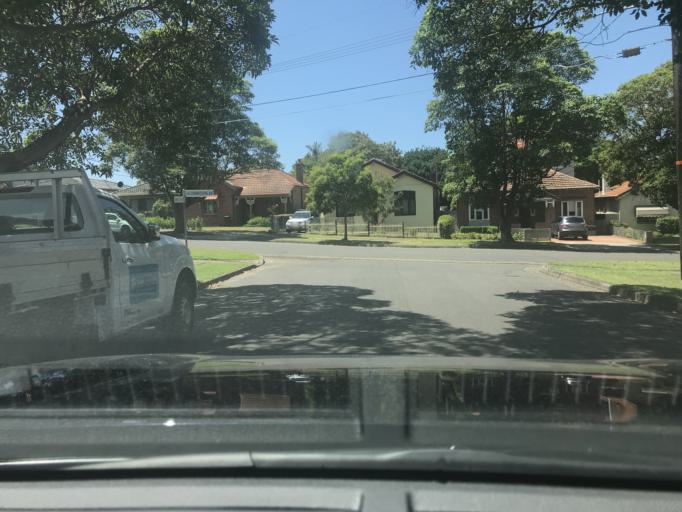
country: AU
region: New South Wales
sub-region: Canada Bay
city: Concord
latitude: -33.8592
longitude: 151.1021
